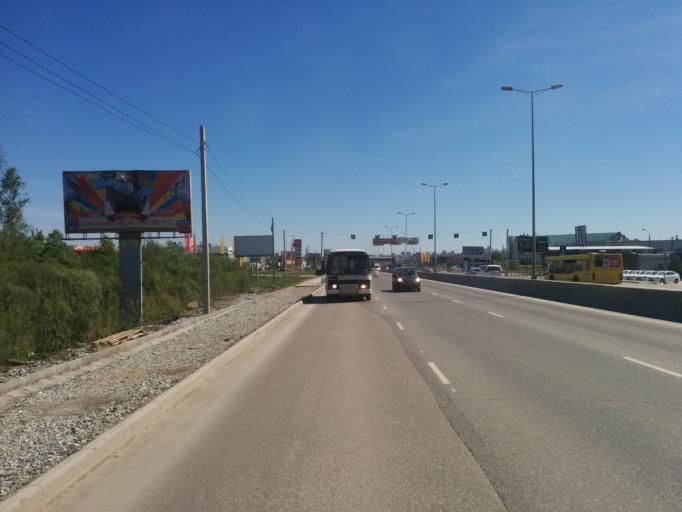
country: RU
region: Perm
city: Perm
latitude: 58.0372
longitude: 56.1940
